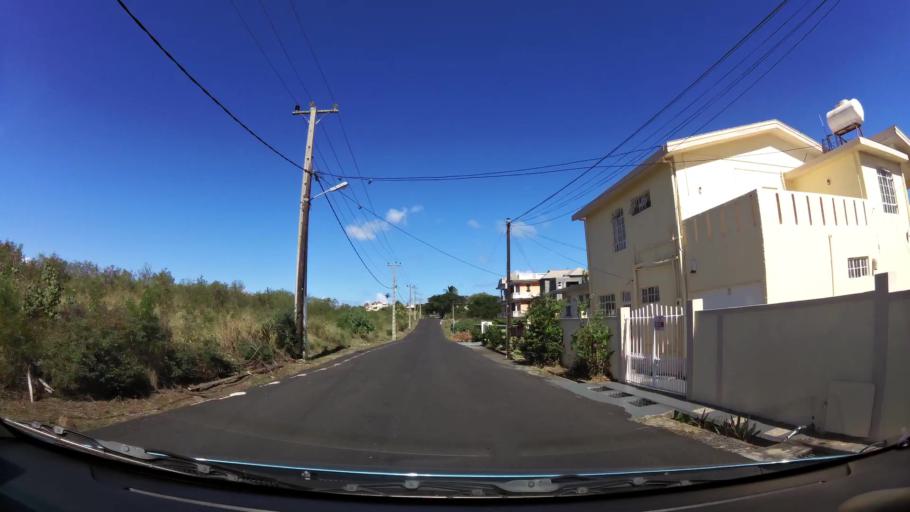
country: MU
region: Black River
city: Flic en Flac
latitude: -20.2659
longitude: 57.3781
